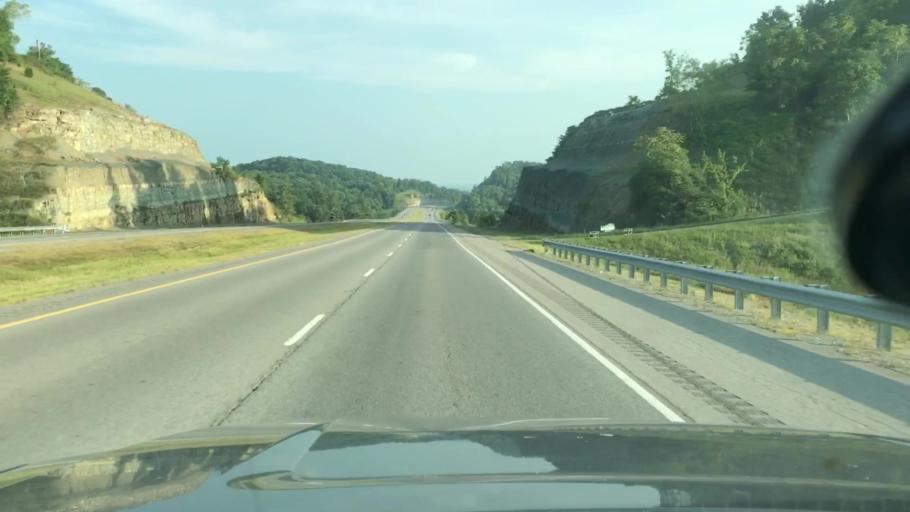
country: US
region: Tennessee
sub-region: Sumner County
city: Gallatin
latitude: 36.4636
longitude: -86.4696
